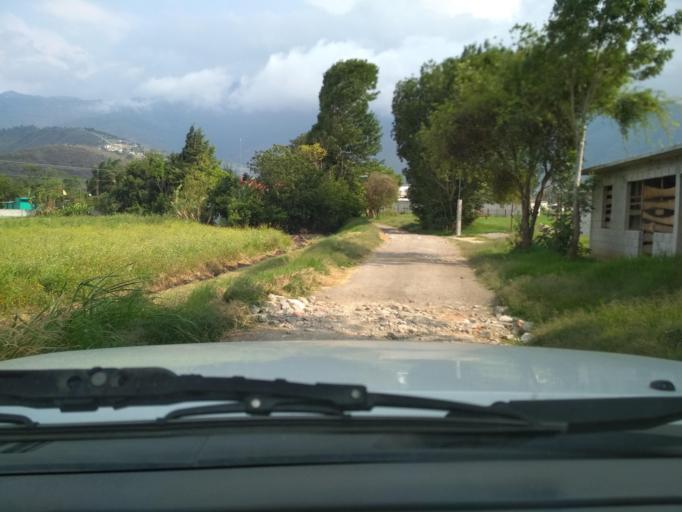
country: MX
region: Veracruz
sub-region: Acultzingo
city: Acatla
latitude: 18.7686
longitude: -97.2250
